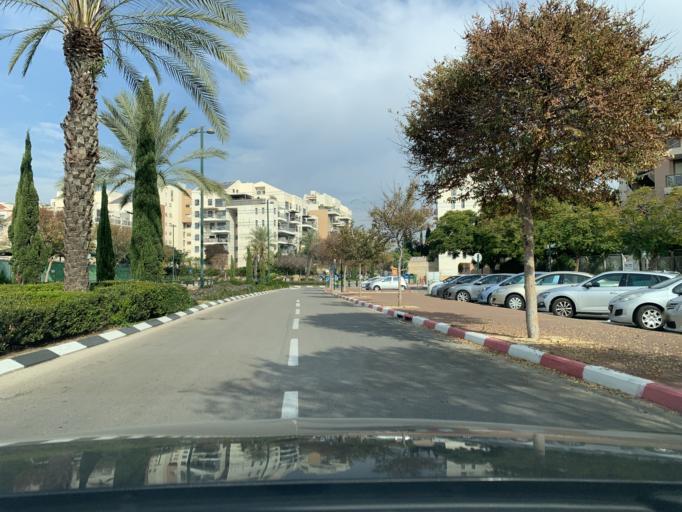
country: IL
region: Central District
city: Kfar Saba
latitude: 32.1842
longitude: 34.9281
